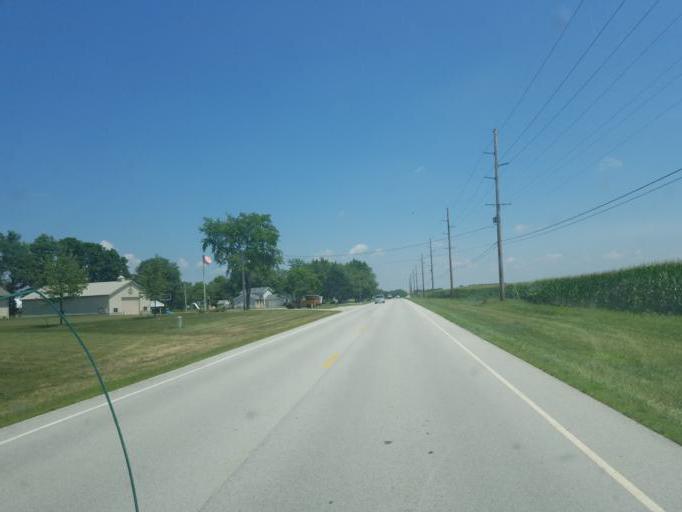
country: US
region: Ohio
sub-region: Auglaize County
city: Saint Marys
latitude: 40.5529
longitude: -84.3215
